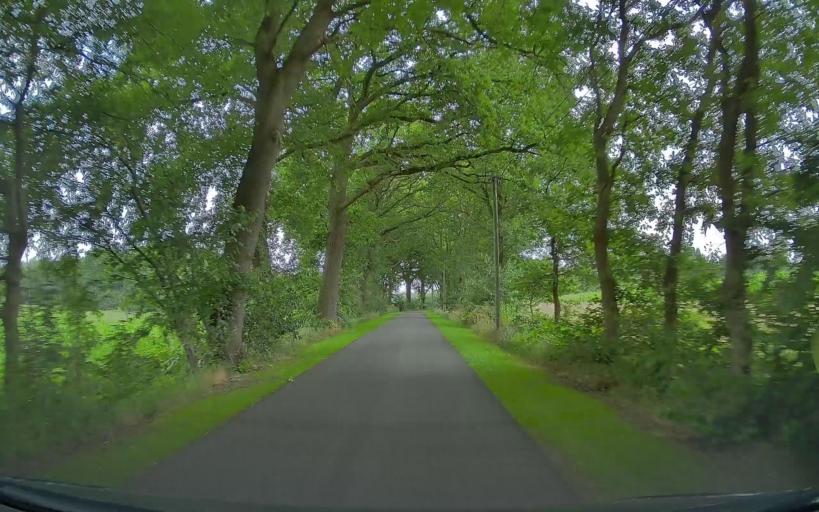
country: DE
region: Lower Saxony
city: Friesoythe
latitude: 52.9960
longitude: 7.8714
